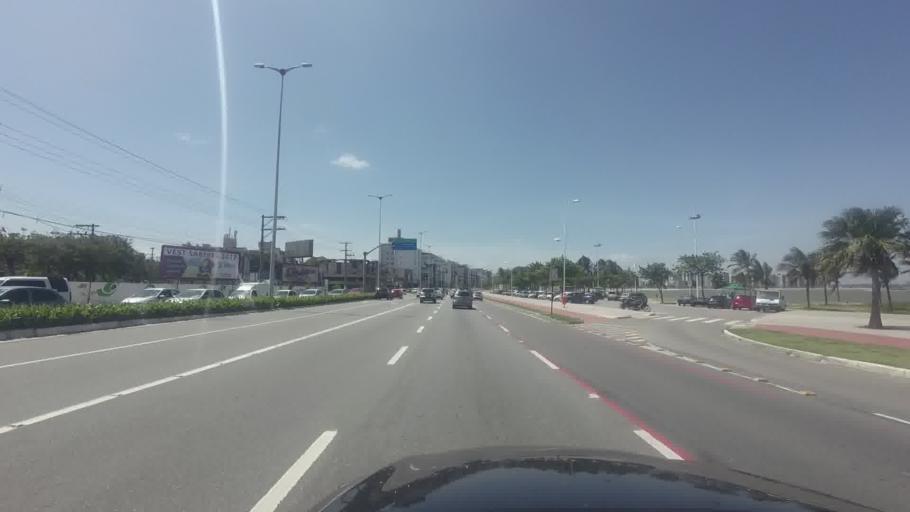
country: BR
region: Espirito Santo
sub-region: Vila Velha
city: Vila Velha
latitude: -20.2930
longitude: -40.2894
